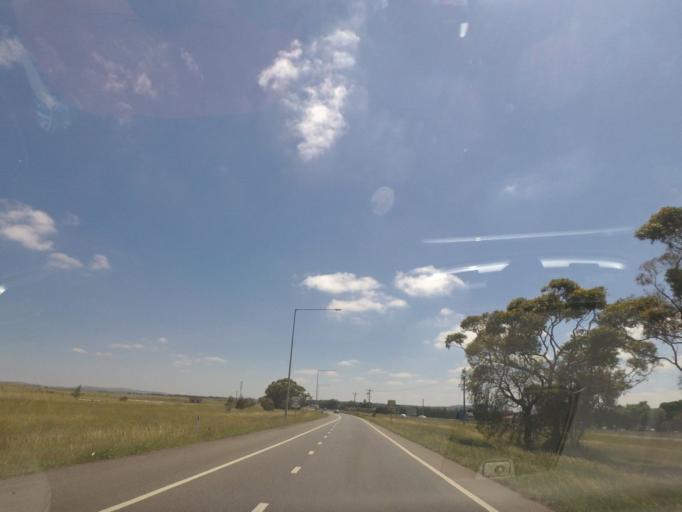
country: AU
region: Victoria
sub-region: Hume
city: Craigieburn
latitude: -37.5369
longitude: 144.9454
